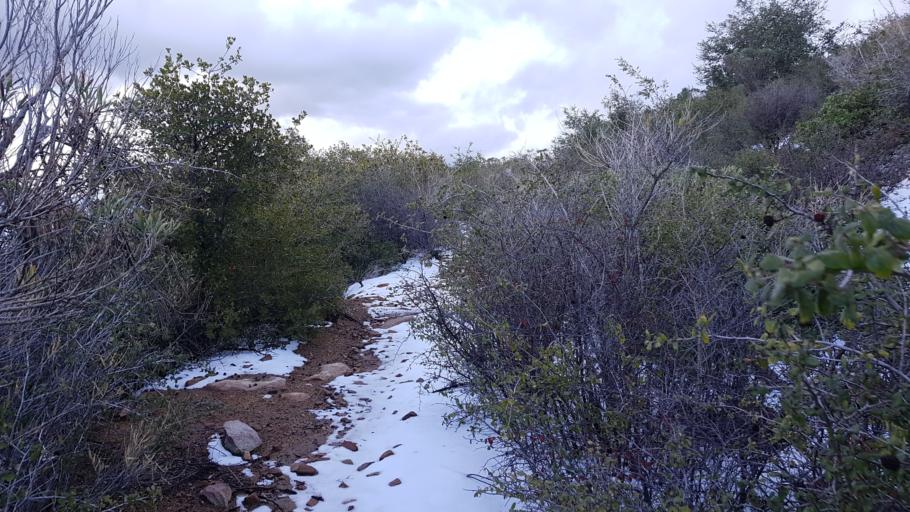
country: US
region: California
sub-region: Riverside County
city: Aguanga
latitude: 33.4131
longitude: -116.9818
